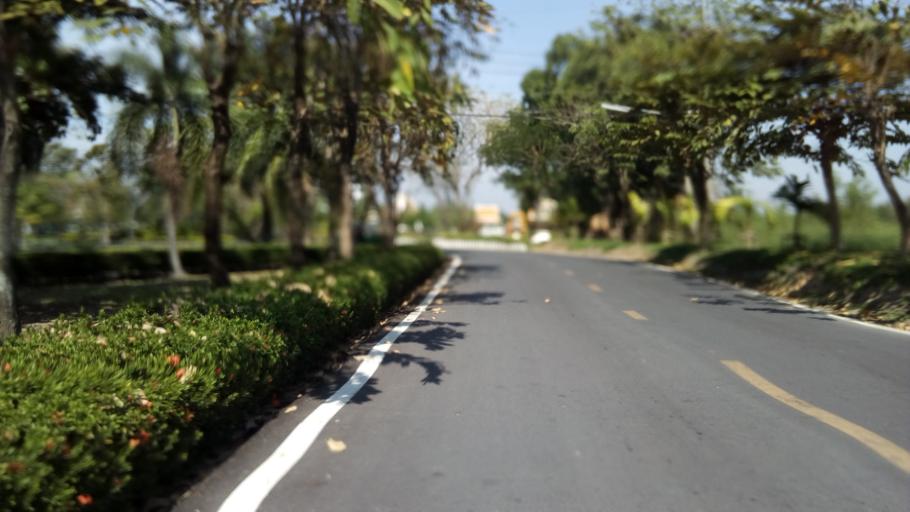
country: TH
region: Pathum Thani
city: Nong Suea
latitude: 14.0656
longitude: 100.8376
